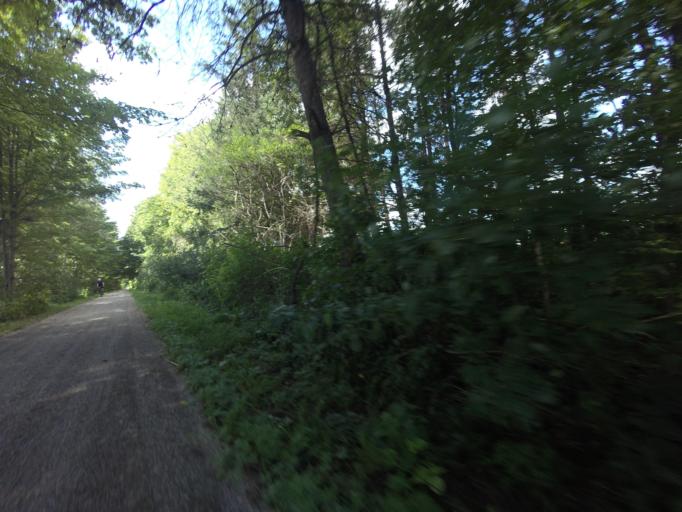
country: CA
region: Ontario
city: Huron East
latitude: 43.6670
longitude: -81.2675
